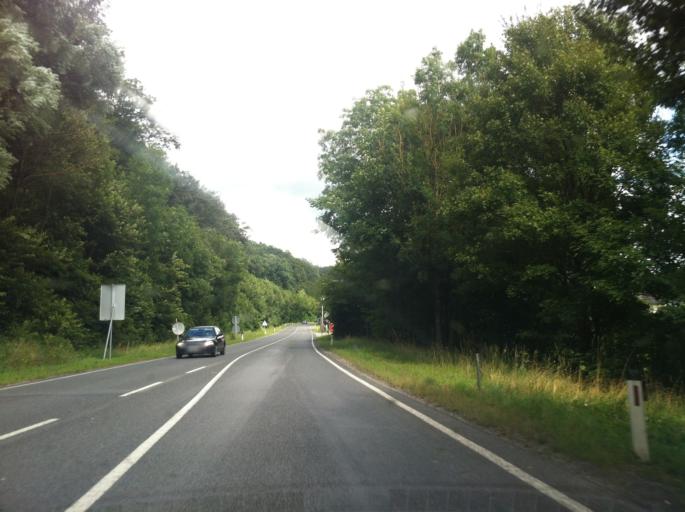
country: AT
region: Lower Austria
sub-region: Politischer Bezirk Wien-Umgebung
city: Gablitz
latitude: 48.2418
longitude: 16.1275
